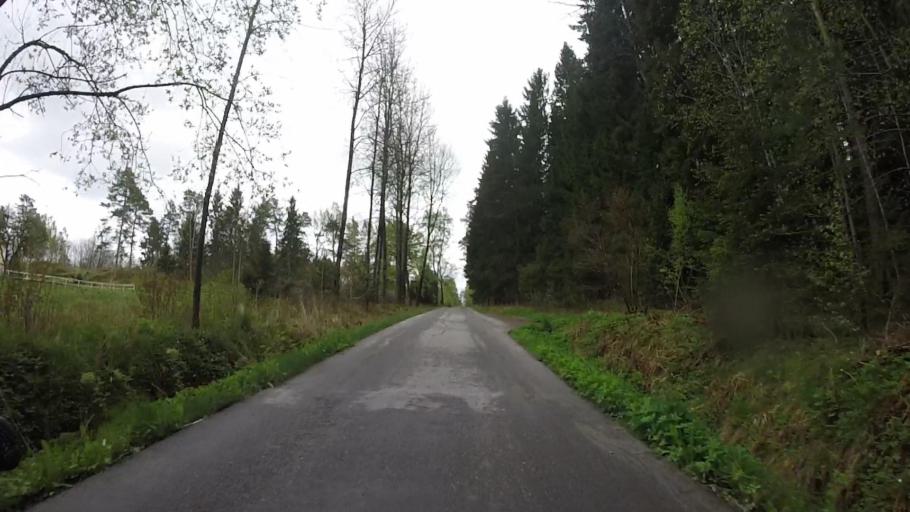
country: SE
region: Vaestra Goetaland
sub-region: Trollhattan
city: Sjuntorp
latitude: 58.2044
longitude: 12.2113
